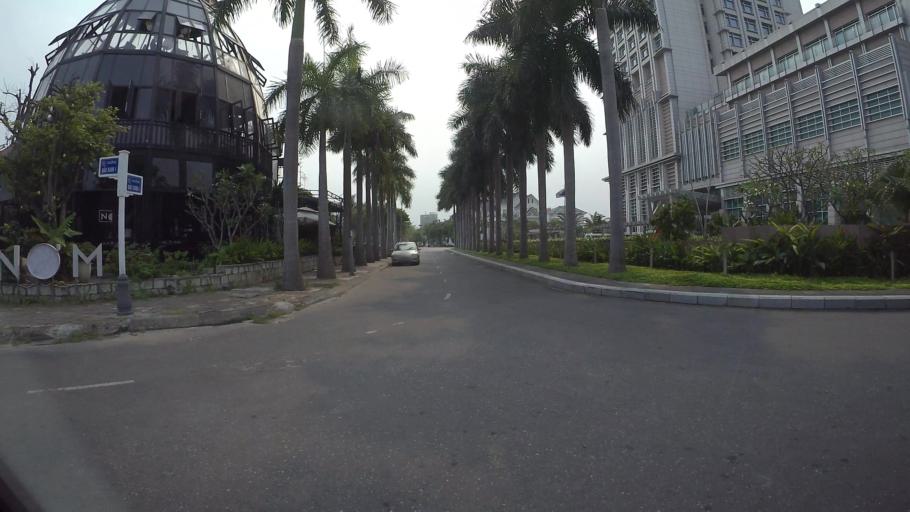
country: VN
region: Da Nang
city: Son Tra
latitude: 16.0481
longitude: 108.2274
